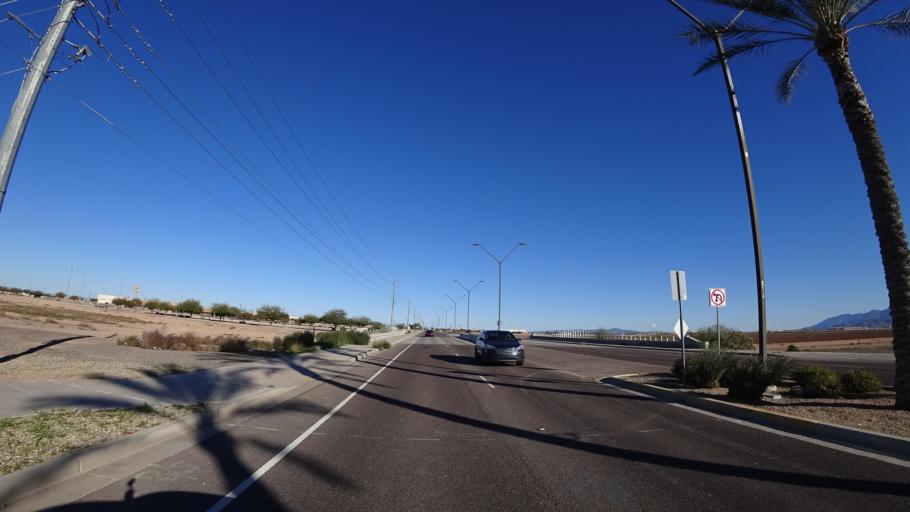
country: US
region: Arizona
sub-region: Maricopa County
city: Goodyear
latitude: 33.4500
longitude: -112.3831
